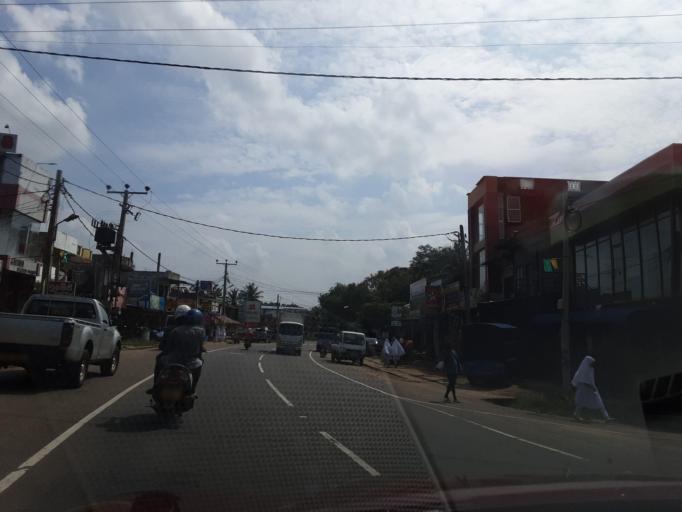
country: LK
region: Northern Province
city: Vavuniya
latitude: 8.5374
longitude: 80.4938
